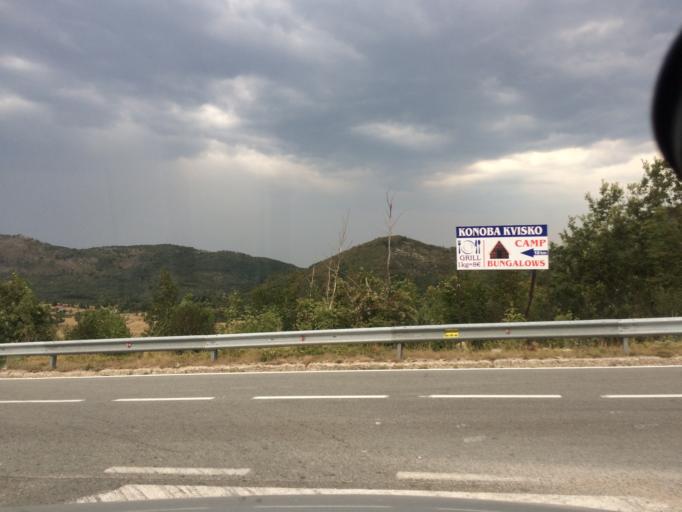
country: ME
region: Opstina Niksic
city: Niksic
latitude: 42.9014
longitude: 18.9601
